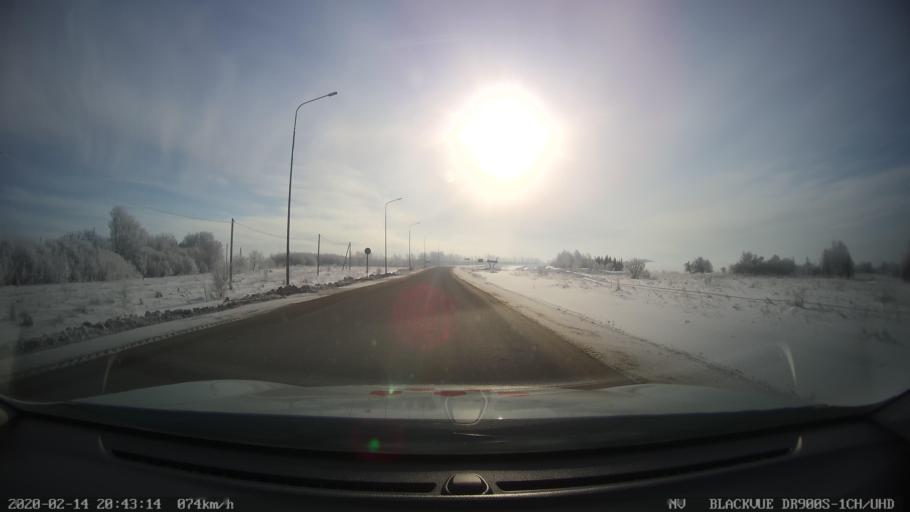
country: RU
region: Tatarstan
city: Kuybyshevskiy Zaton
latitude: 55.3102
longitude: 49.1462
